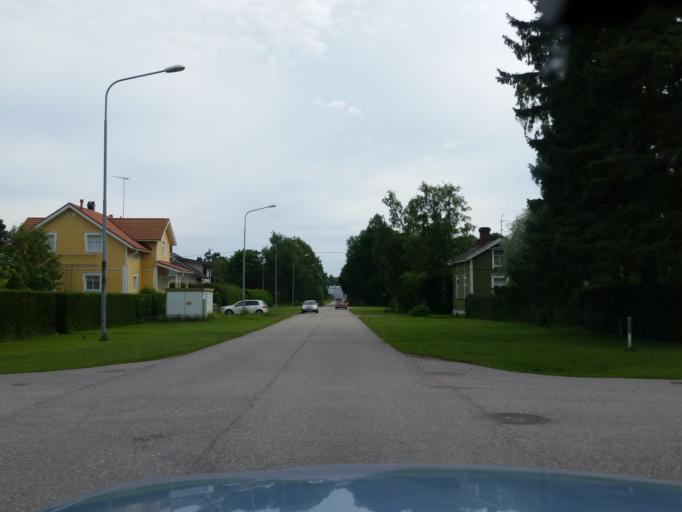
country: FI
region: Uusimaa
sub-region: Raaseporin
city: Hanko
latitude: 59.8327
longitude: 22.9539
